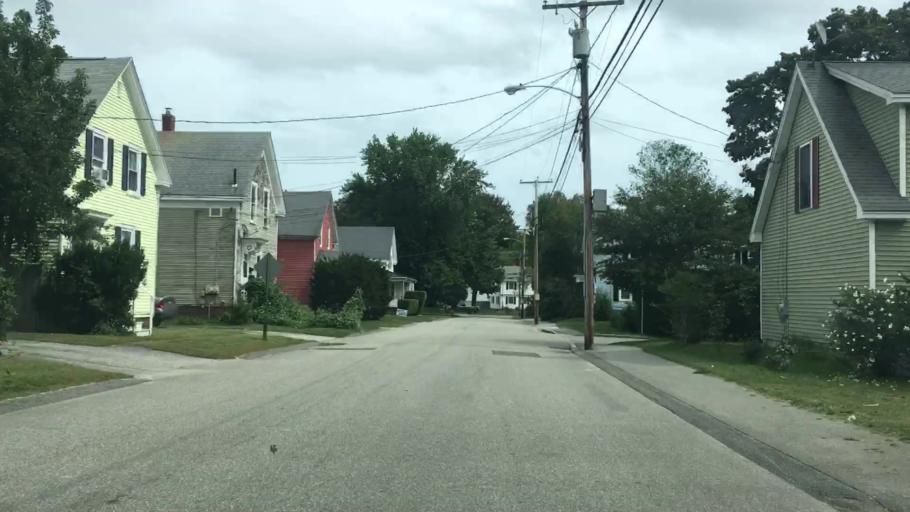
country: US
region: Maine
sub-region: Cumberland County
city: Westbrook
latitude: 43.6725
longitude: -70.3634
